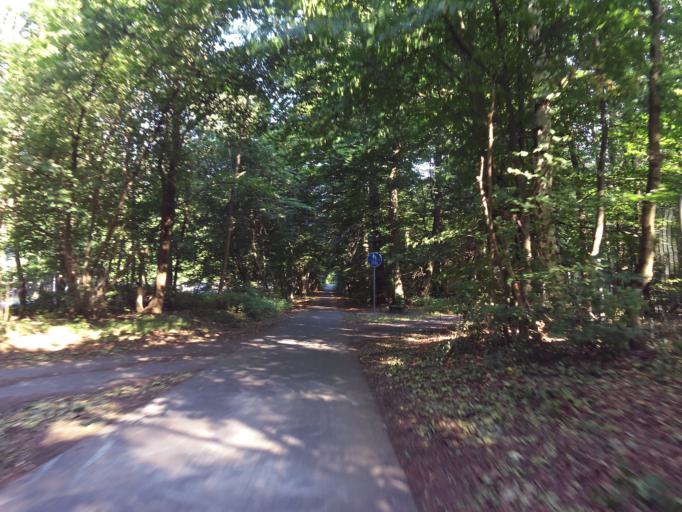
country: DE
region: Hesse
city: Raunheim
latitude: 49.9874
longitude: 8.4761
